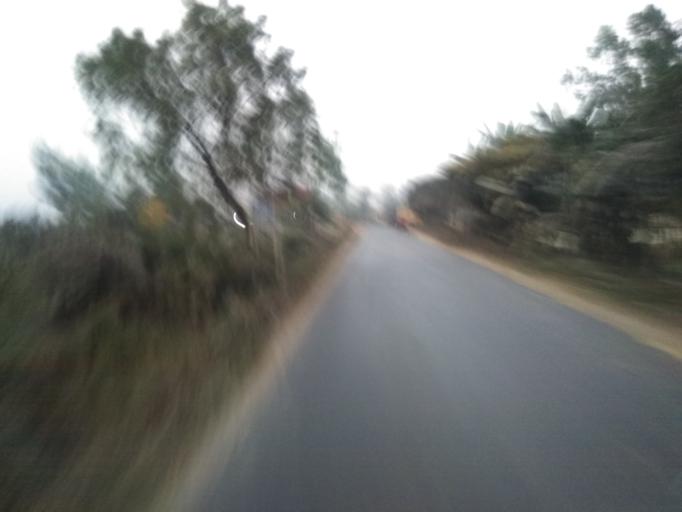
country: BD
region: Rajshahi
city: Bogra
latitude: 24.7383
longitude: 89.3309
